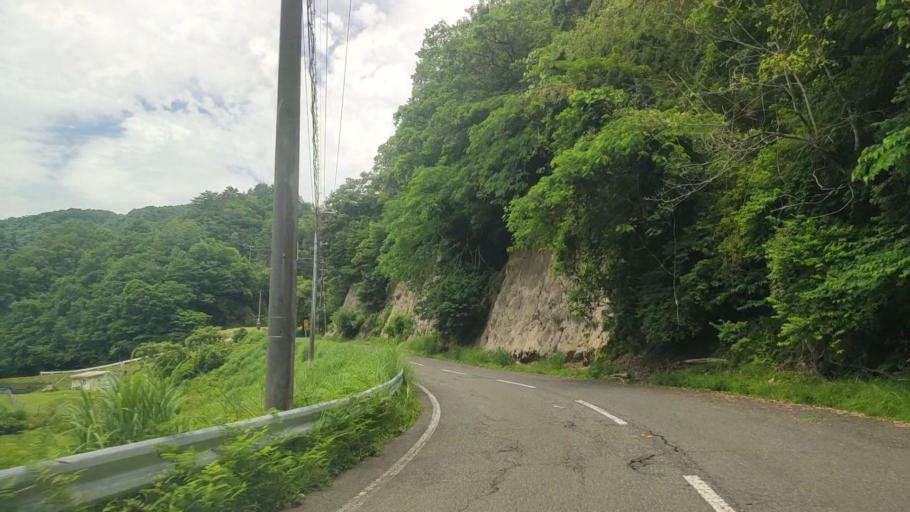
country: JP
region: Hyogo
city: Toyooka
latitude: 35.5219
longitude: 134.6964
